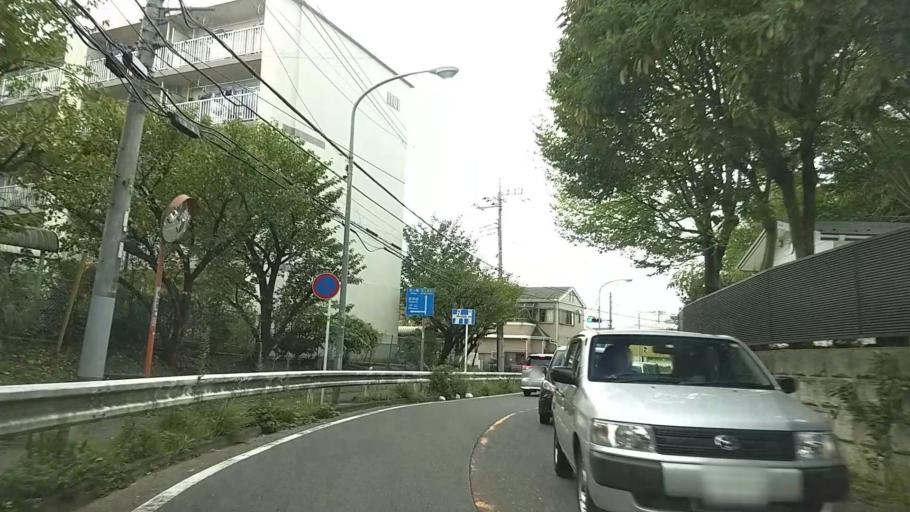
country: JP
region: Kanagawa
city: Yokohama
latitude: 35.5032
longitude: 139.5639
